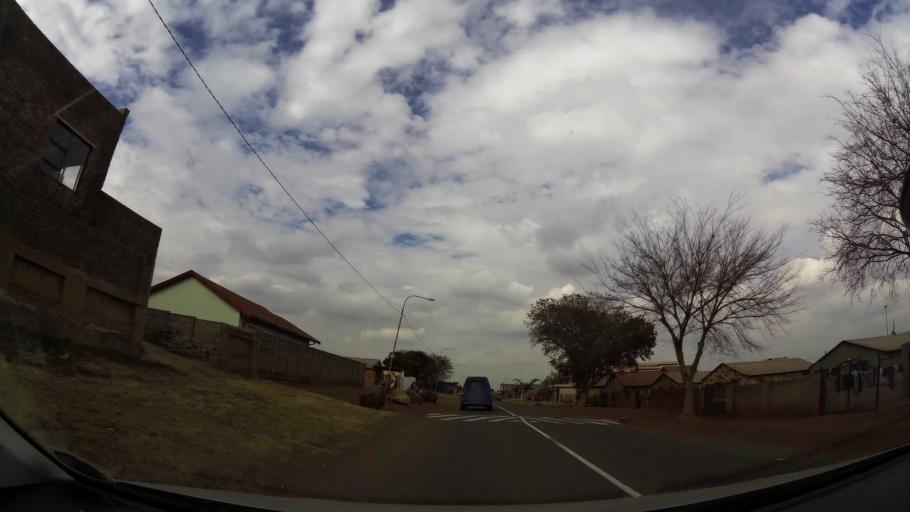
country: ZA
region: Gauteng
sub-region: City of Johannesburg Metropolitan Municipality
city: Soweto
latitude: -26.2750
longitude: 27.8469
